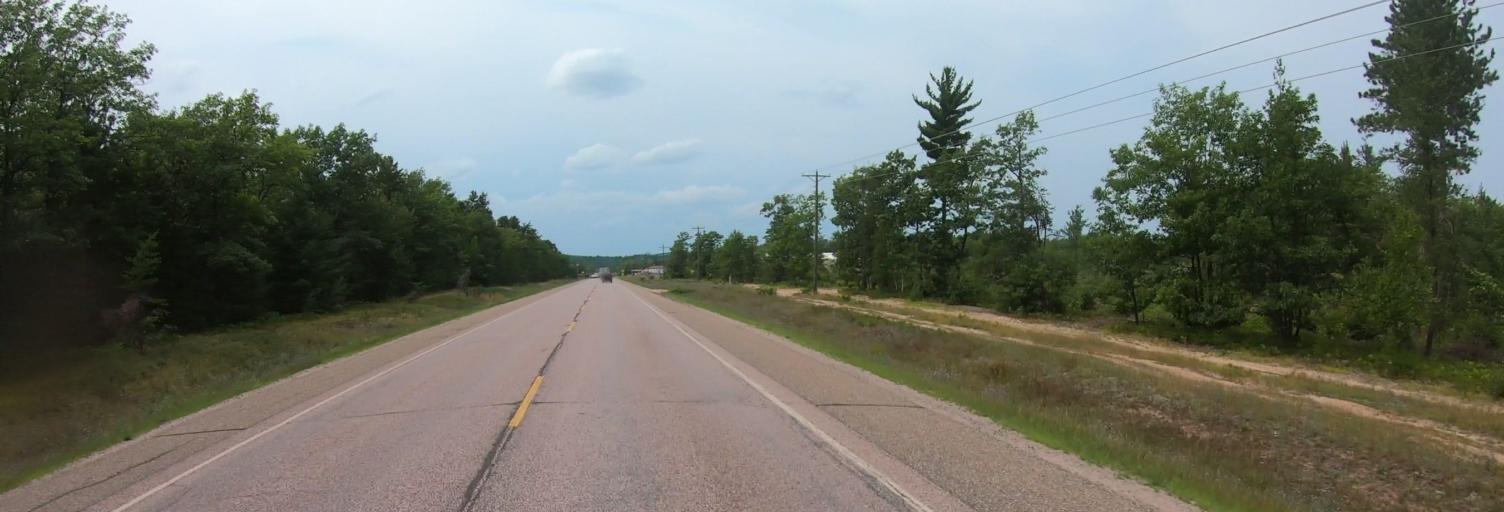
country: US
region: Michigan
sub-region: Marquette County
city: Harvey
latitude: 46.4615
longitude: -87.4185
